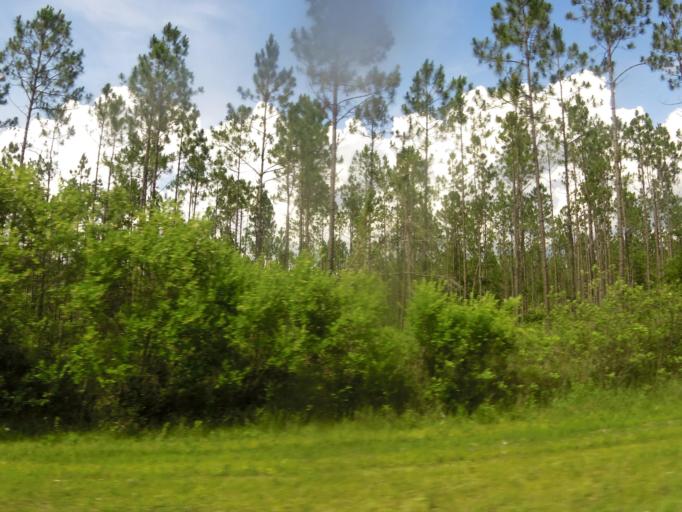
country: US
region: Florida
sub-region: Baker County
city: Macclenny
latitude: 30.2569
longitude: -82.0906
